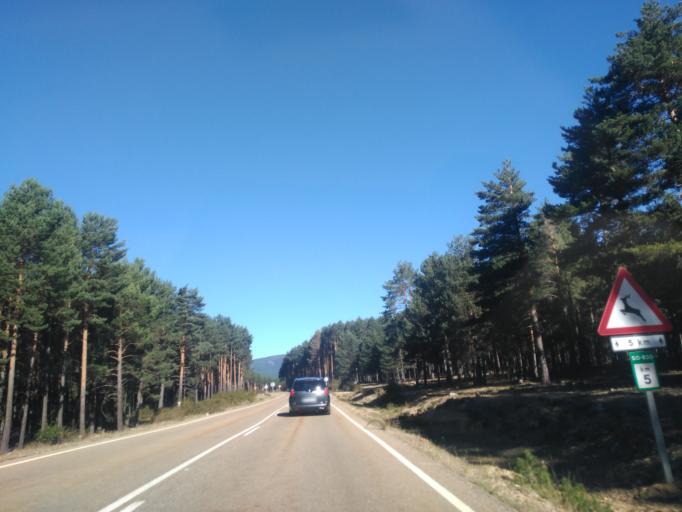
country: ES
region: Castille and Leon
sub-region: Provincia de Soria
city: Vinuesa
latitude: 41.9521
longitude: -2.7743
